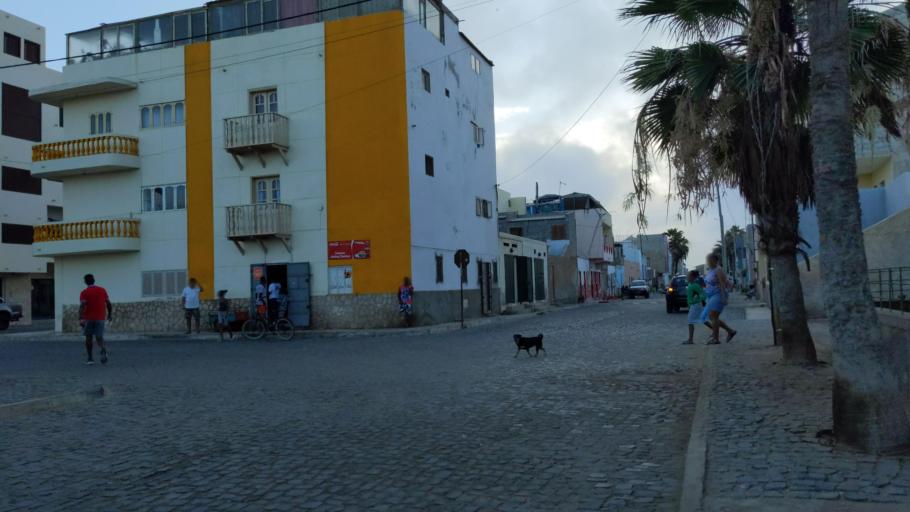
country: CV
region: Sal
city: Santa Maria
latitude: 16.5997
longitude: -22.9032
